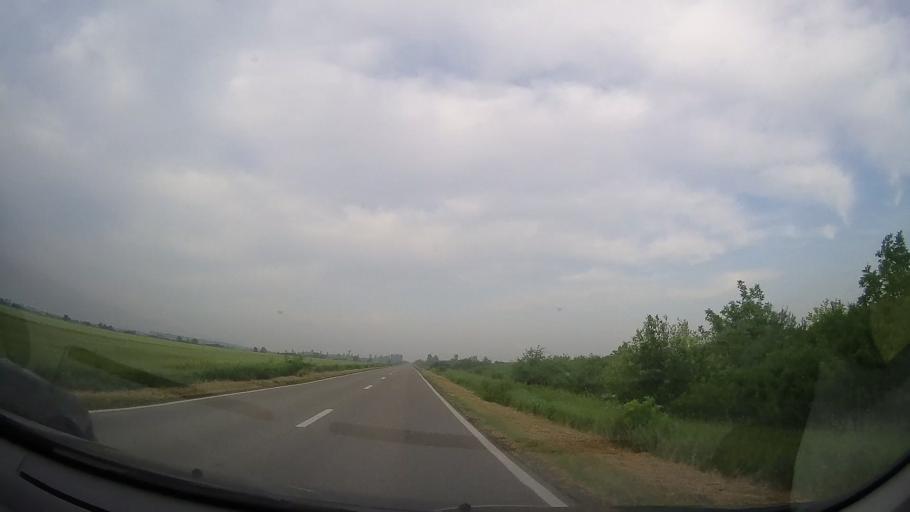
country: RO
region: Timis
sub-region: Comuna Parta
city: Parta
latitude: 45.6408
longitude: 21.1218
